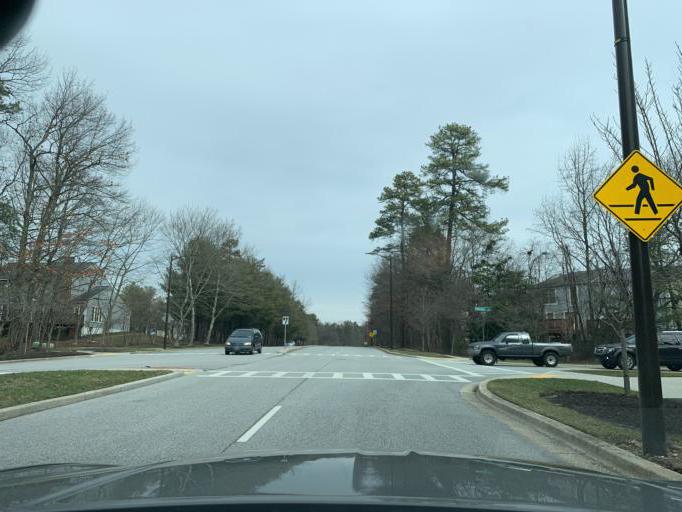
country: US
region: Maryland
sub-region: Anne Arundel County
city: Maryland City
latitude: 39.1046
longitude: -76.8055
